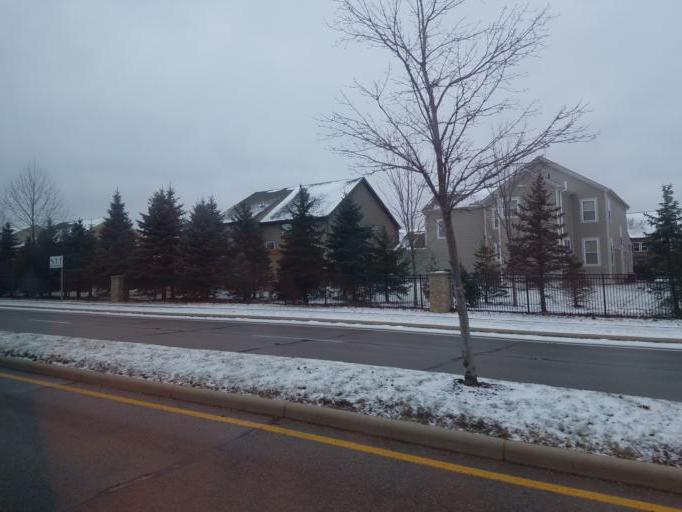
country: US
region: Ohio
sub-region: Franklin County
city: Worthington
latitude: 40.1166
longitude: -83.0465
